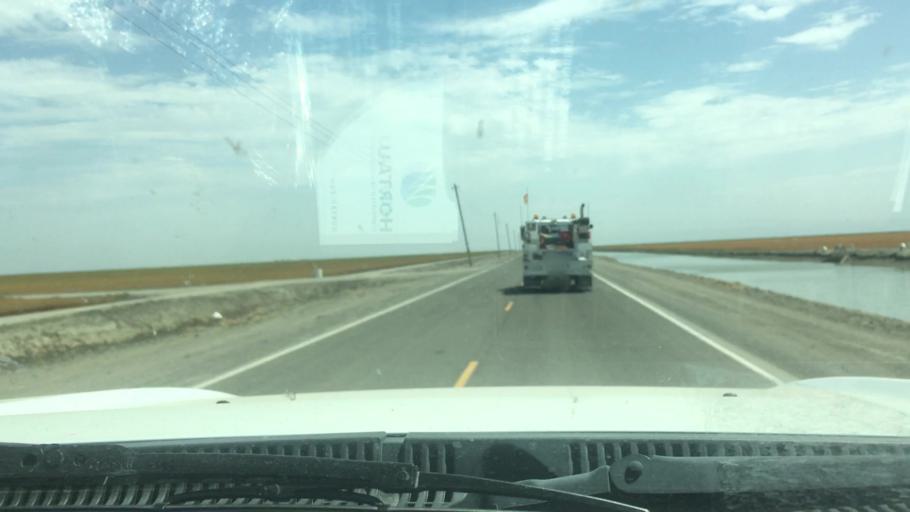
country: US
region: California
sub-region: Tulare County
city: Alpaugh
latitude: 35.9210
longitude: -119.5733
